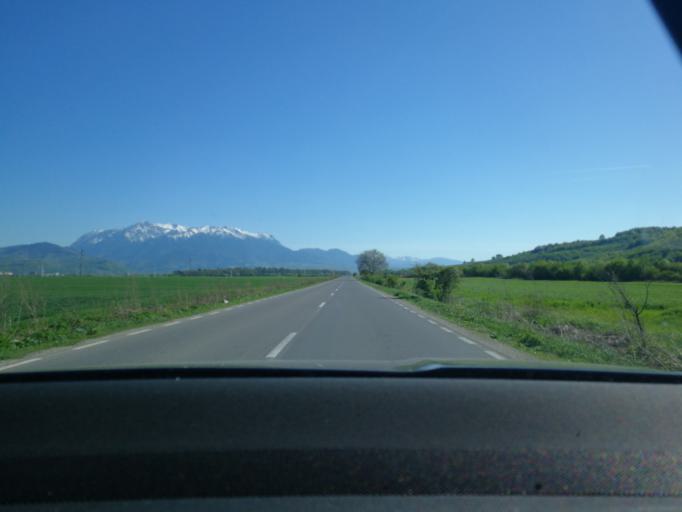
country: RO
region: Brasov
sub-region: Comuna Vulcan
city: Vulcan
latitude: 45.6134
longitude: 25.4233
